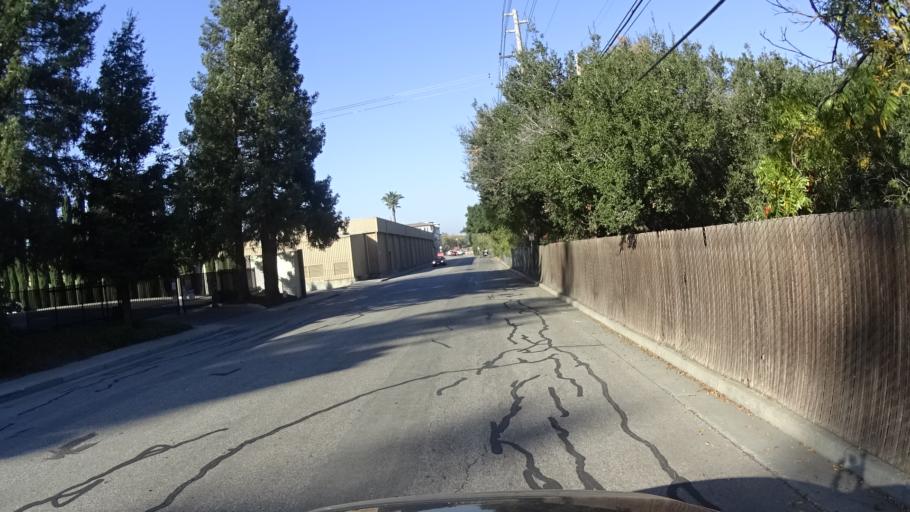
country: US
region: California
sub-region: Santa Clara County
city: Santa Clara
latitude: 37.3503
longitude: -121.9734
